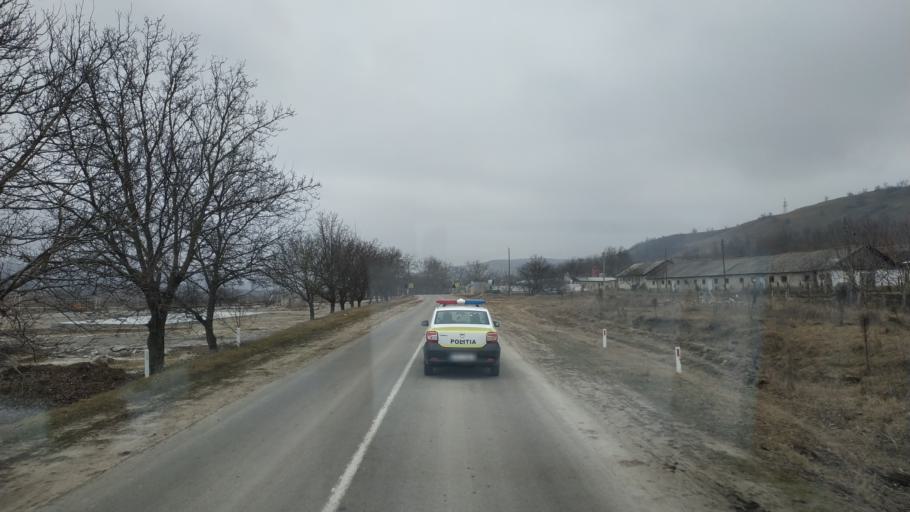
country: MD
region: Hincesti
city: Hincesti
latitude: 46.9694
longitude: 28.4763
